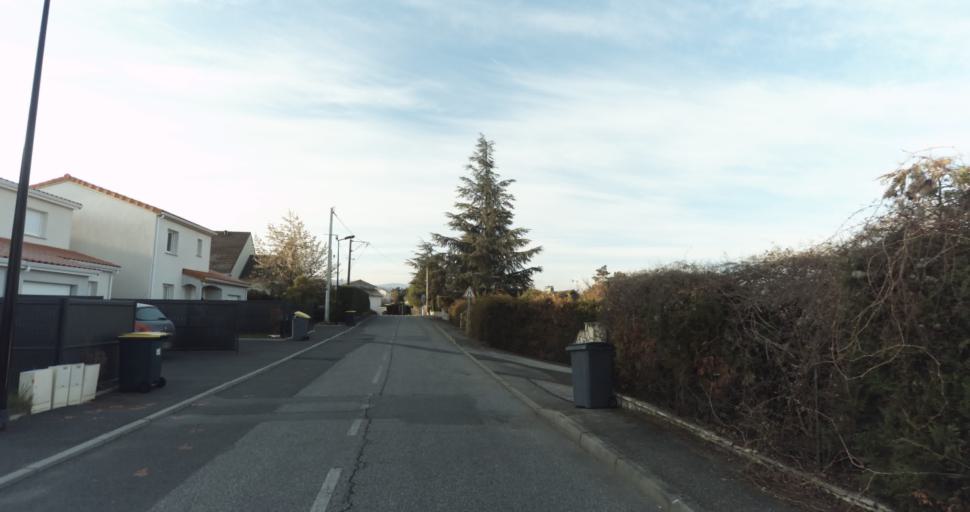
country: FR
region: Rhone-Alpes
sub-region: Departement de la Loire
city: Saint-Jean-Bonnefonds
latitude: 45.4523
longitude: 4.4277
